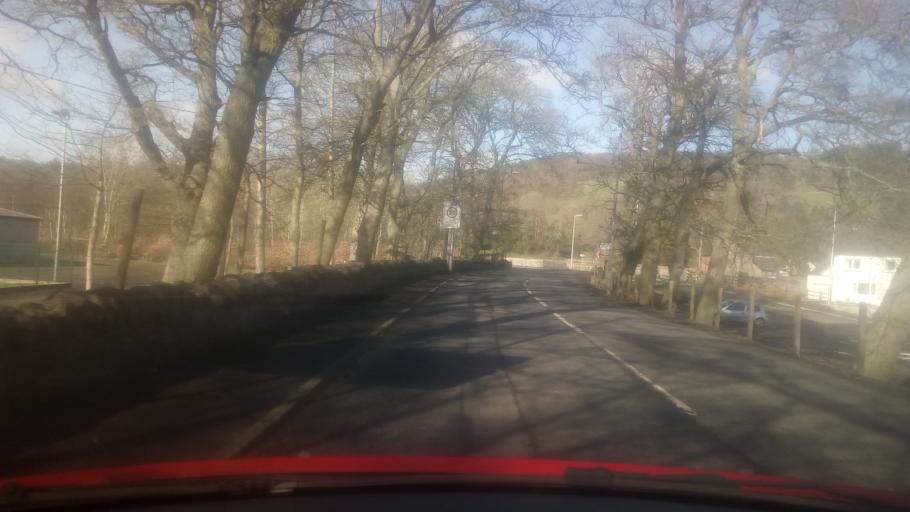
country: GB
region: Scotland
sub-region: The Scottish Borders
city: Selkirk
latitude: 55.5481
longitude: -2.8559
